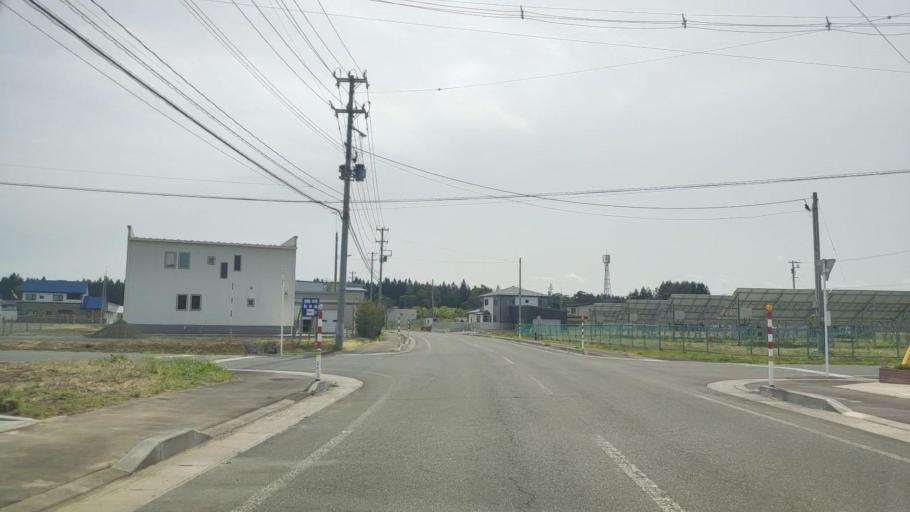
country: JP
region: Aomori
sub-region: Misawa Shi
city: Inuotose
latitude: 40.7186
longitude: 141.1507
